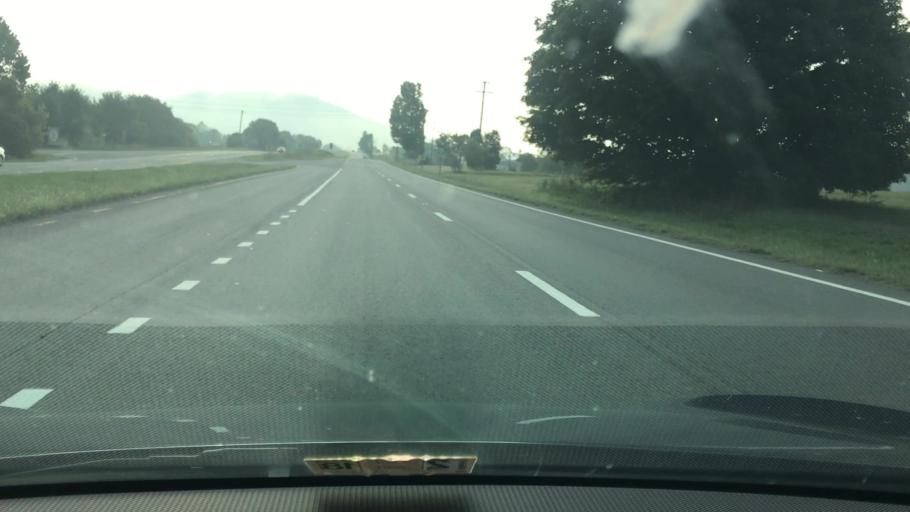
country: US
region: Virginia
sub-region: Botetourt County
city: Blue Ridge
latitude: 37.3792
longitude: -79.7184
